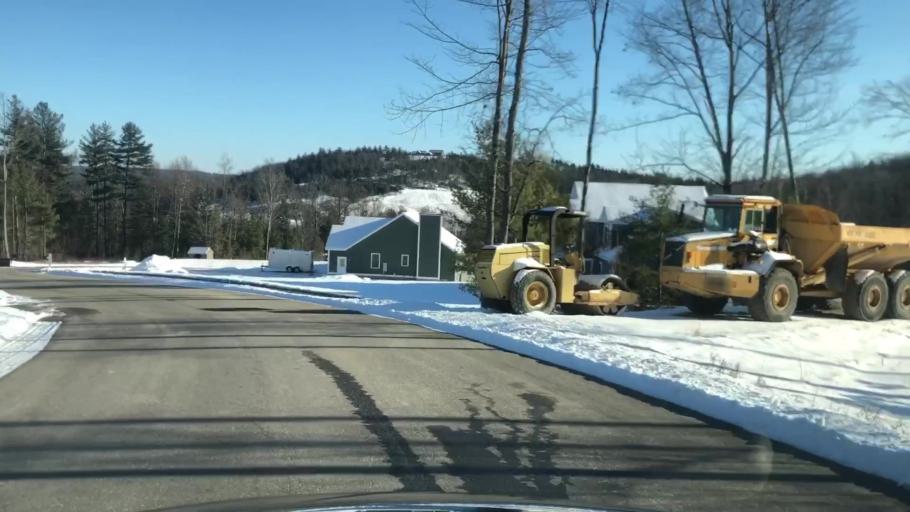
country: US
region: New Hampshire
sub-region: Hillsborough County
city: Wilton
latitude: 42.8027
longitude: -71.7099
